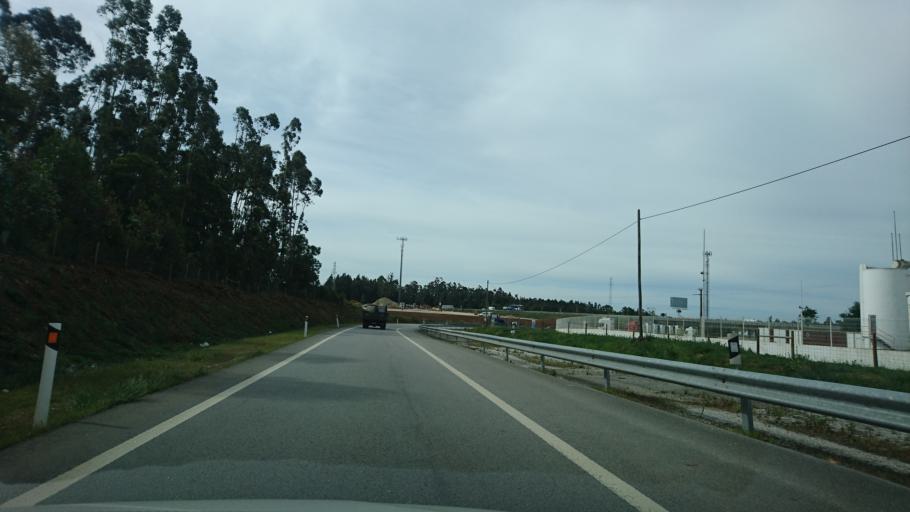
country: PT
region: Aveiro
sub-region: Albergaria-A-Velha
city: Albergaria-a-Velha
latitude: 40.6901
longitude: -8.5193
